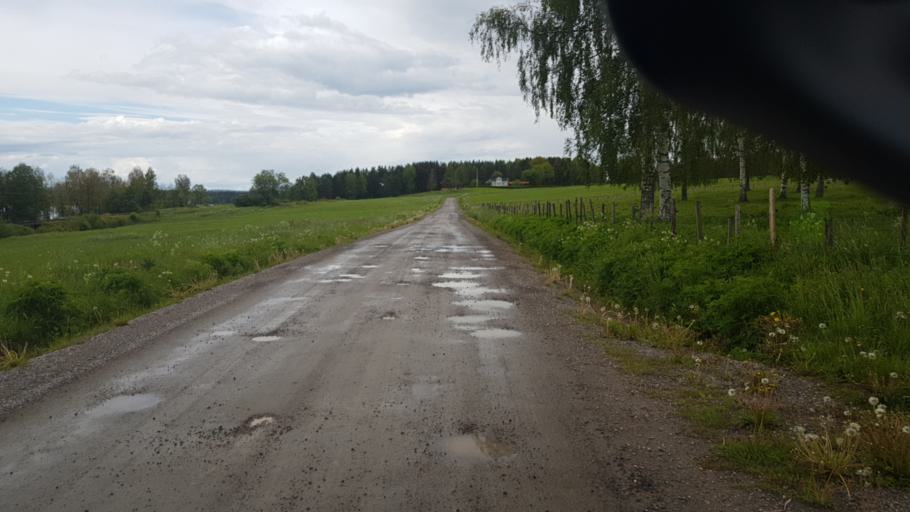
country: SE
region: Vaermland
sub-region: Eda Kommun
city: Amotfors
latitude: 59.8051
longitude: 12.3632
